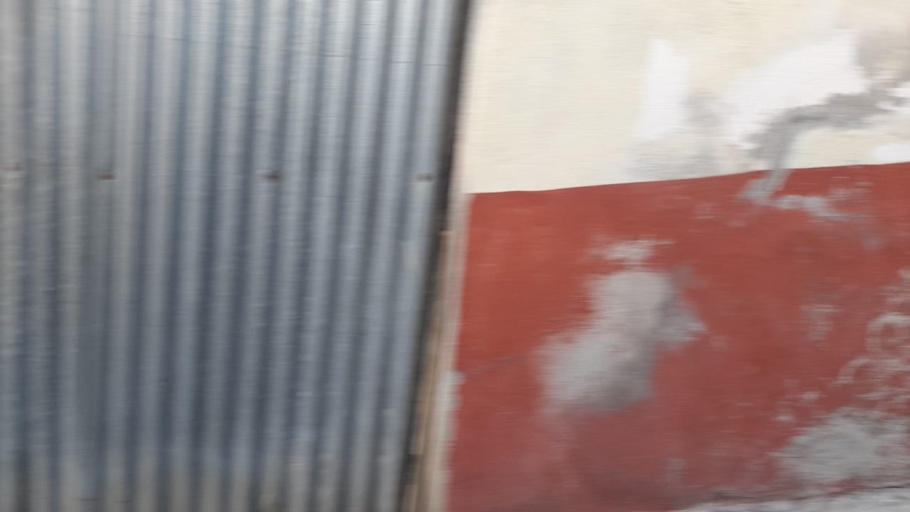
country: GT
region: Quetzaltenango
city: Quetzaltenango
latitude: 14.8289
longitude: -91.5175
